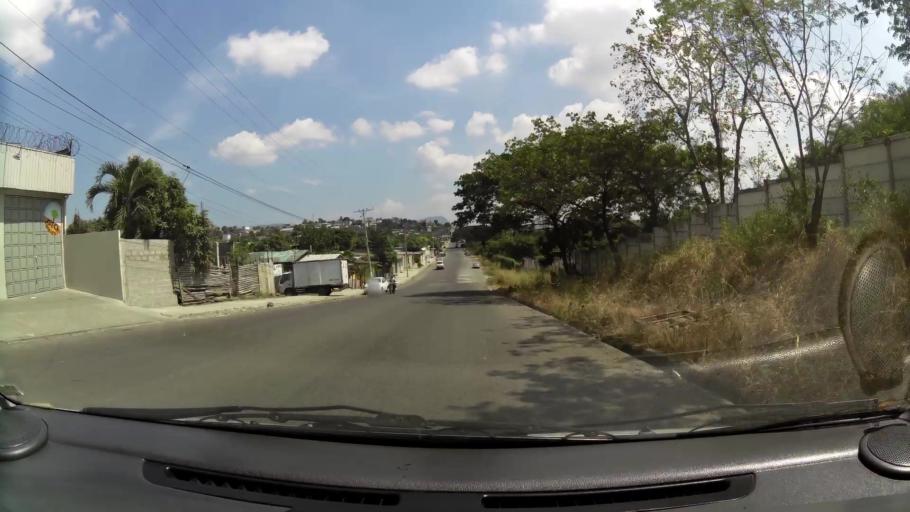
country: EC
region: Guayas
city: Eloy Alfaro
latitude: -2.1119
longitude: -79.9141
